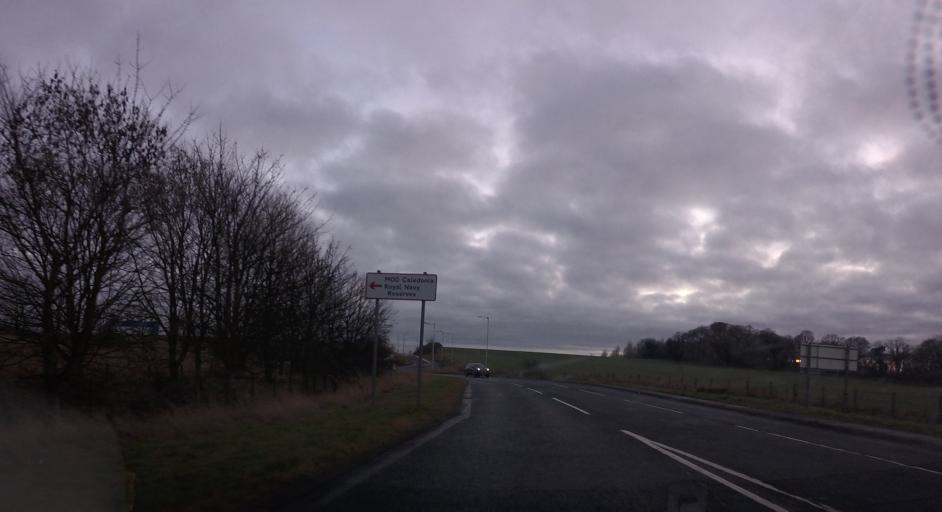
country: GB
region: Scotland
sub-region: Fife
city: Limekilns
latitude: 56.0351
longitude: -3.4580
